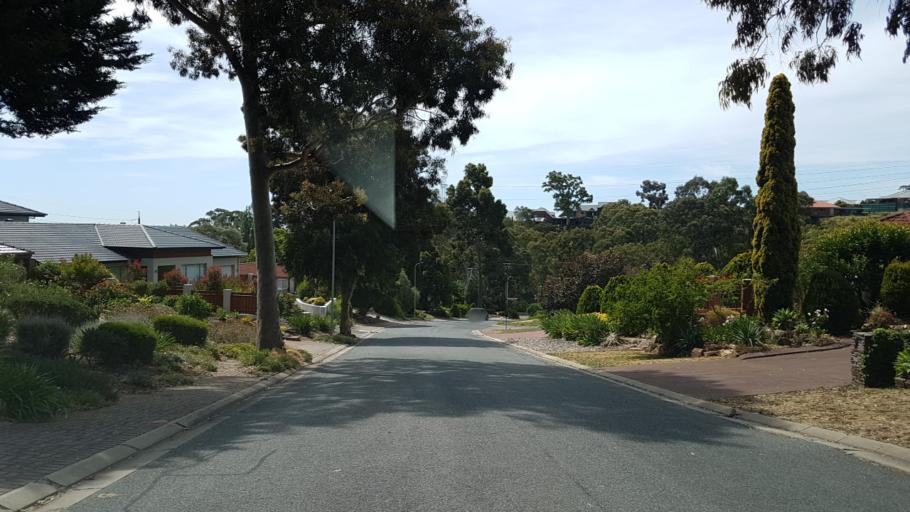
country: AU
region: South Australia
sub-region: Burnside
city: Wattle Park
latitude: -34.9142
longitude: 138.6864
